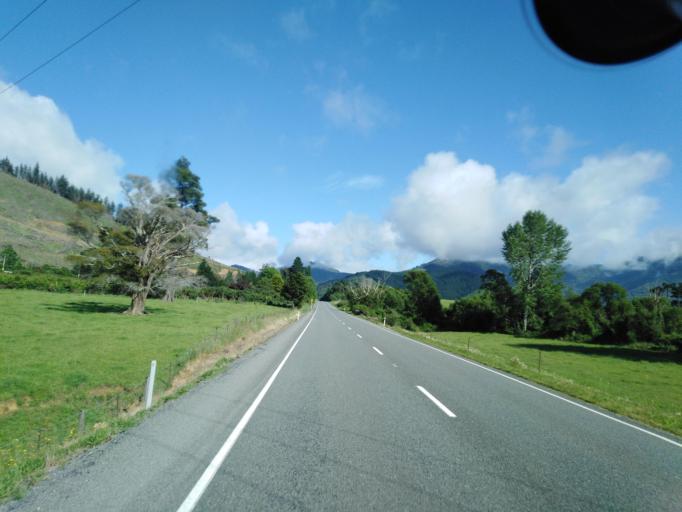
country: NZ
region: Marlborough
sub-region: Marlborough District
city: Picton
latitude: -41.2870
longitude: 173.6639
